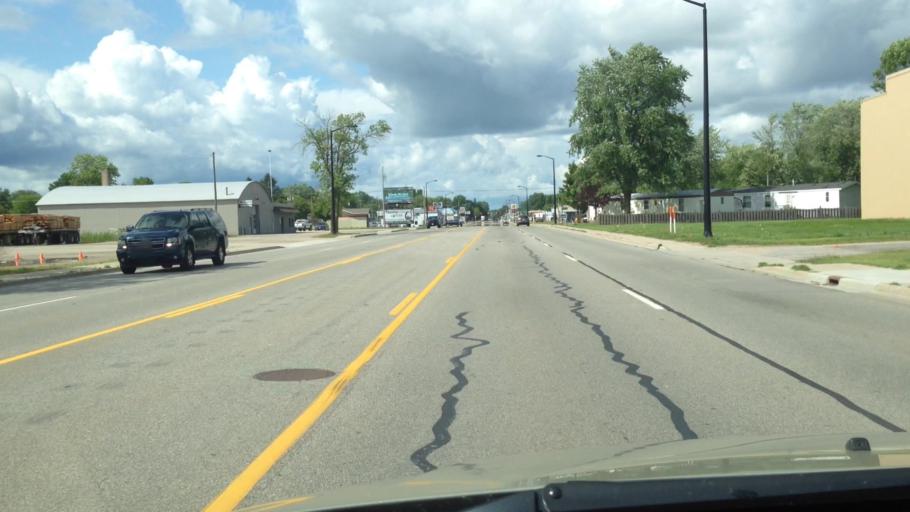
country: US
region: Michigan
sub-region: Menominee County
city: Menominee
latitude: 45.1279
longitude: -87.6129
